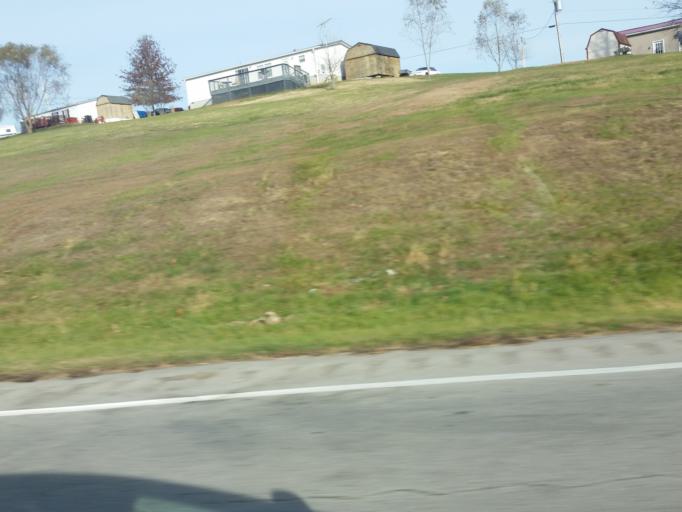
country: US
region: Kentucky
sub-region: Pendleton County
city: Falmouth
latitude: 38.5721
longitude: -84.2965
